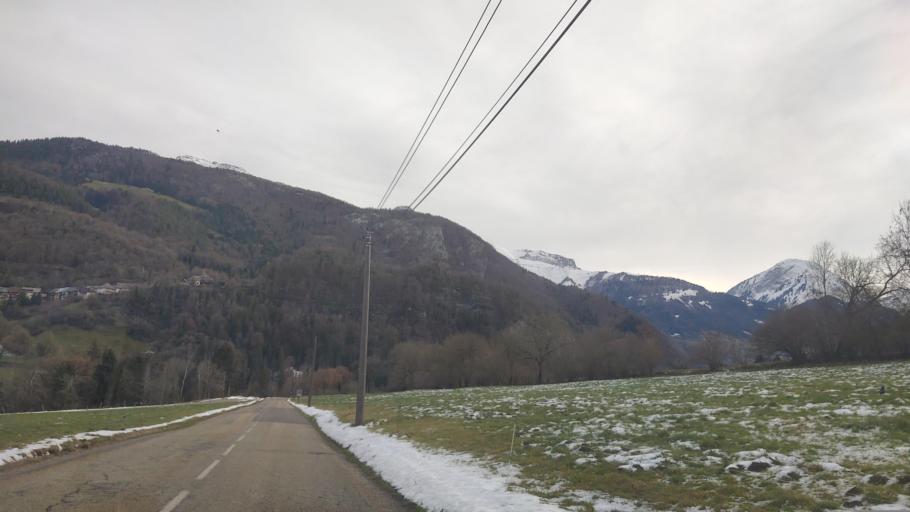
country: FR
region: Rhone-Alpes
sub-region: Departement de la Haute-Savoie
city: Gruffy
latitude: 45.6794
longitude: 6.1268
